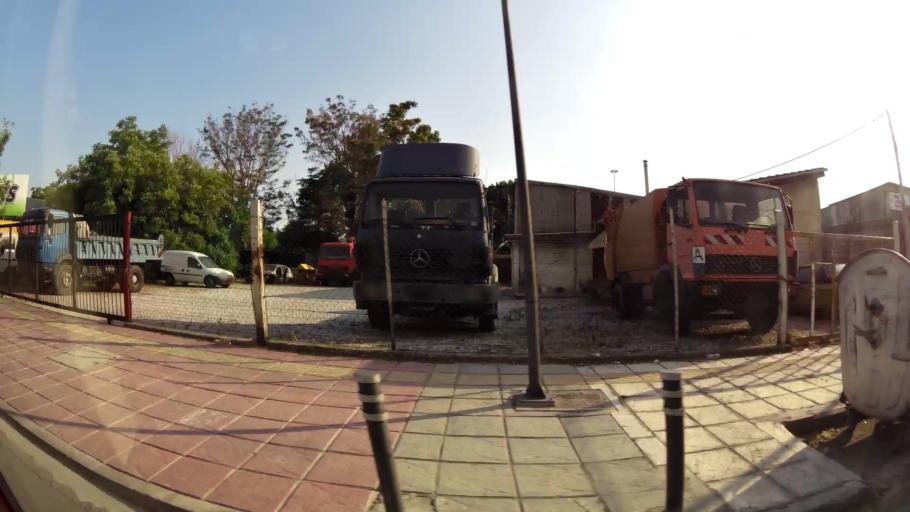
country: GR
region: Central Macedonia
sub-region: Nomos Thessalonikis
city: Menemeni
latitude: 40.6672
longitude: 22.8905
